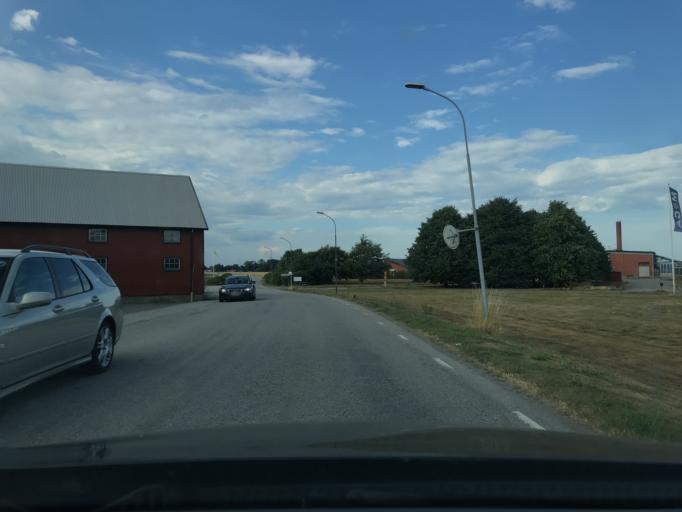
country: SE
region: Skane
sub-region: Tomelilla Kommun
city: Tomelilla
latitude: 55.5068
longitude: 14.1523
